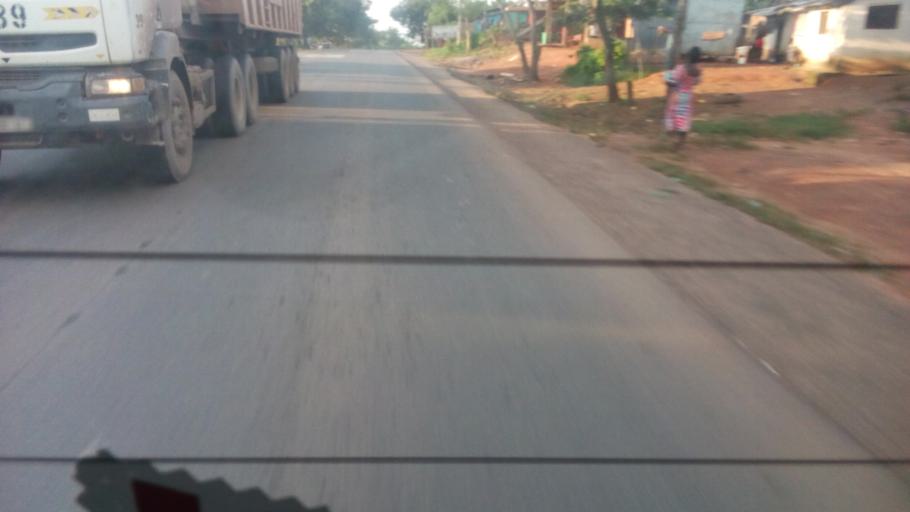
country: GH
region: Western
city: Tarkwa
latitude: 5.1584
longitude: -2.0751
